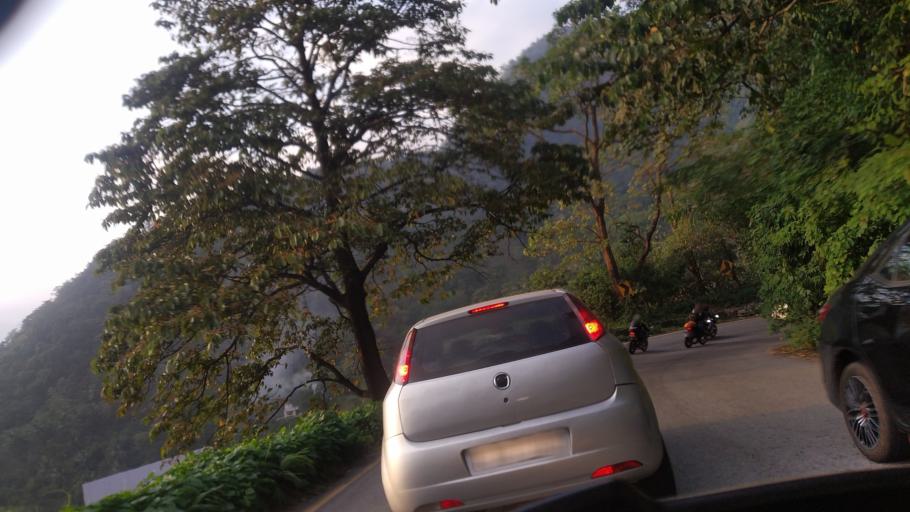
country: IN
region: Kerala
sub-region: Wayanad
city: Kalpetta
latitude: 11.5030
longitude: 76.0241
